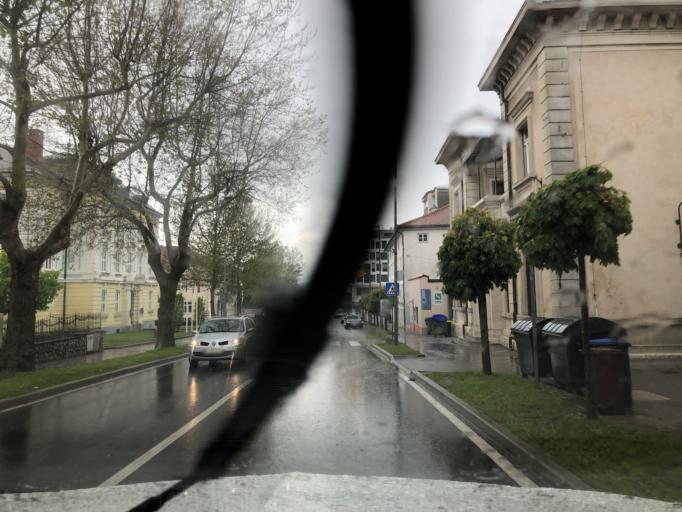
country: SI
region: Postojna
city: Postojna
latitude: 45.7758
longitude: 14.2144
